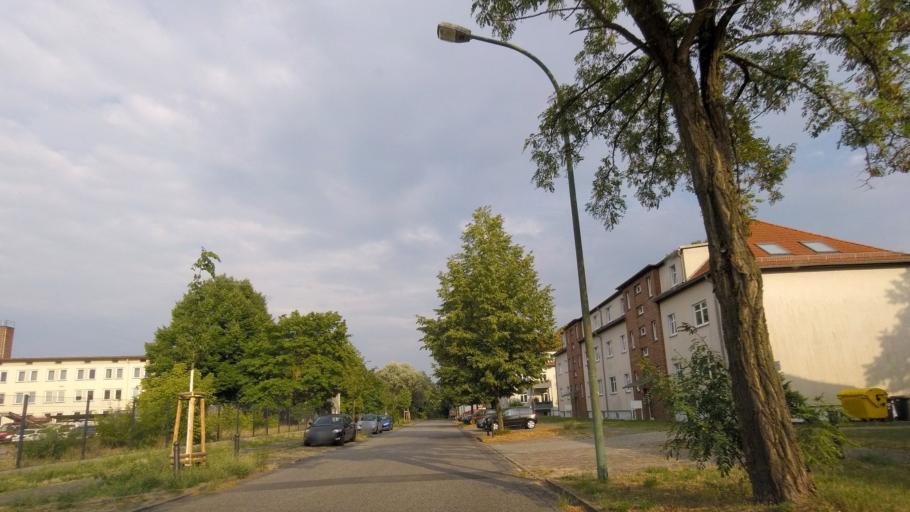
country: DE
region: Brandenburg
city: Potsdam
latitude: 52.3824
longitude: 13.1098
